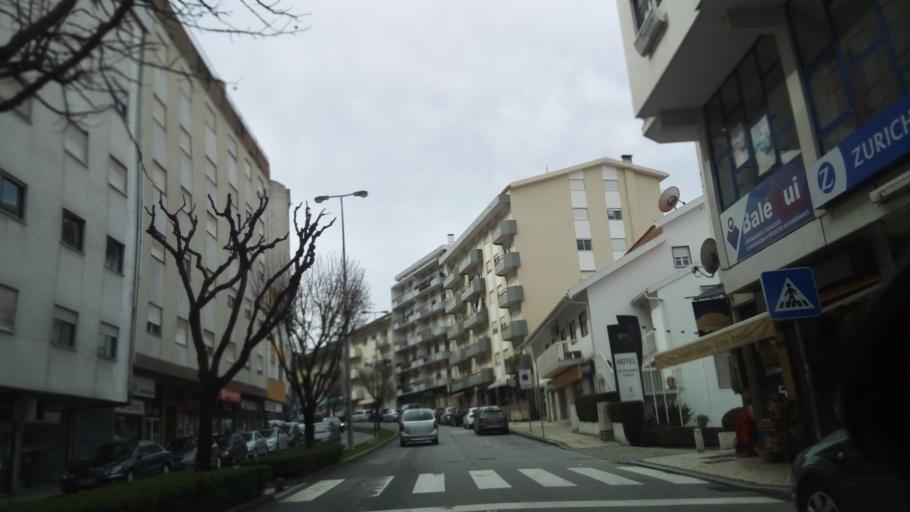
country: PT
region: Guarda
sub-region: Seia
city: Seia
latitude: 40.4184
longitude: -7.7043
